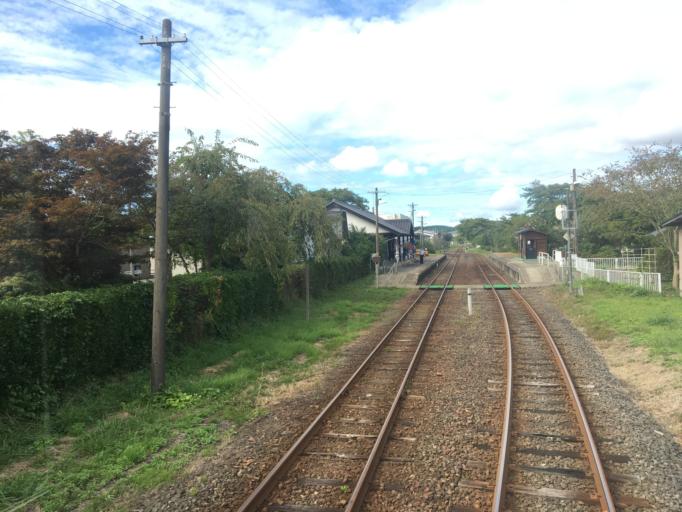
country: JP
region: Yamagata
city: Yuza
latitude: 39.3122
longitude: 140.1131
